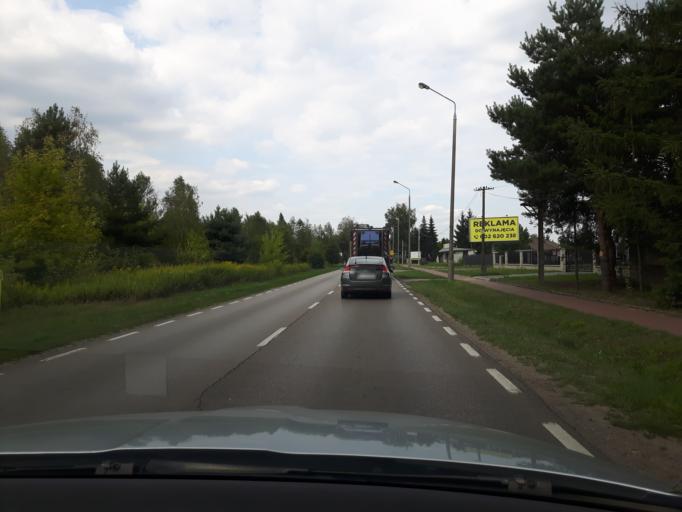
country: PL
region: Masovian Voivodeship
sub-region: Powiat legionowski
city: Stanislawow Pierwszy
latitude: 52.3922
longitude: 21.0331
